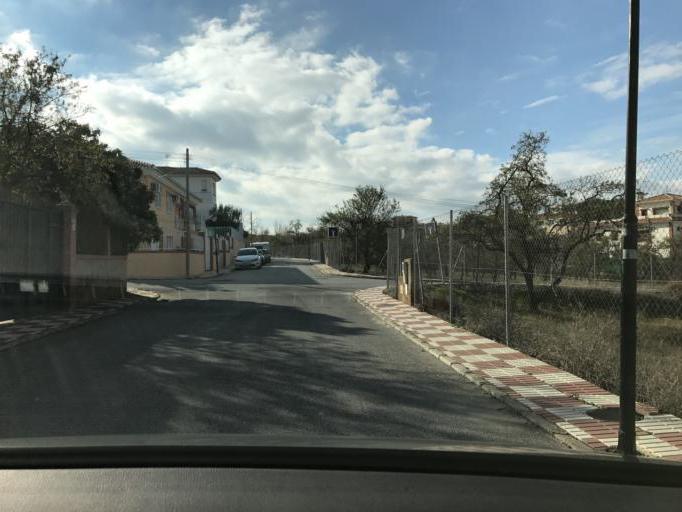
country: ES
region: Andalusia
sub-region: Provincia de Granada
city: Otura
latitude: 37.0858
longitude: -3.6293
